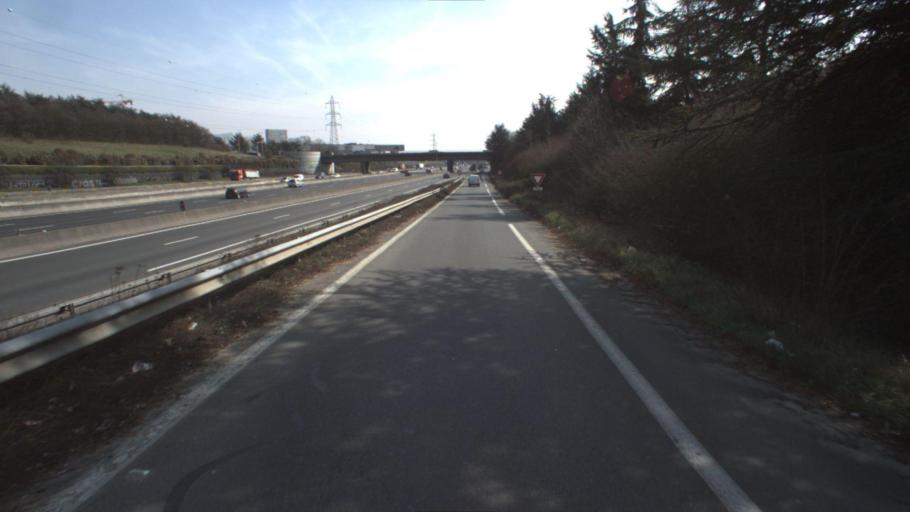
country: FR
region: Ile-de-France
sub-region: Departement de l'Essonne
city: Courcouronnes
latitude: 48.6251
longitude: 2.4169
